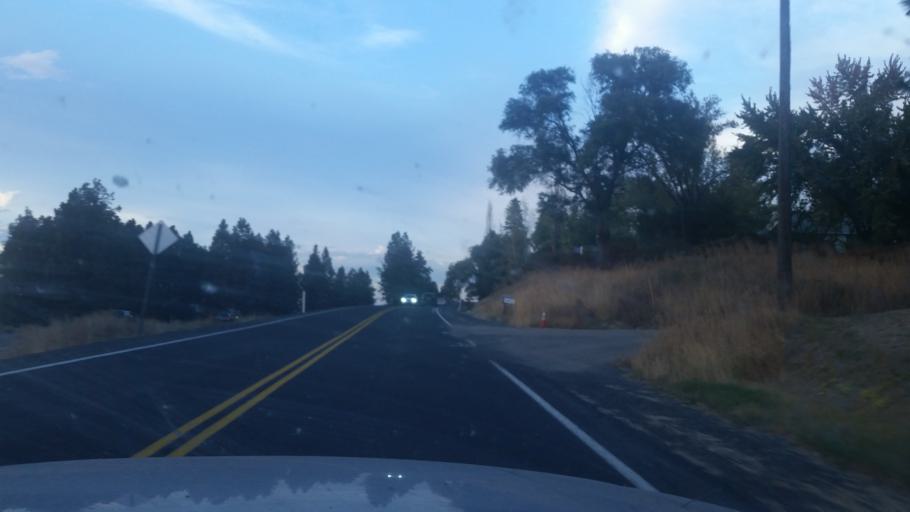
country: US
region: Washington
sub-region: Spokane County
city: Fairchild Air Force Base
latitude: 47.5638
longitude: -117.5933
